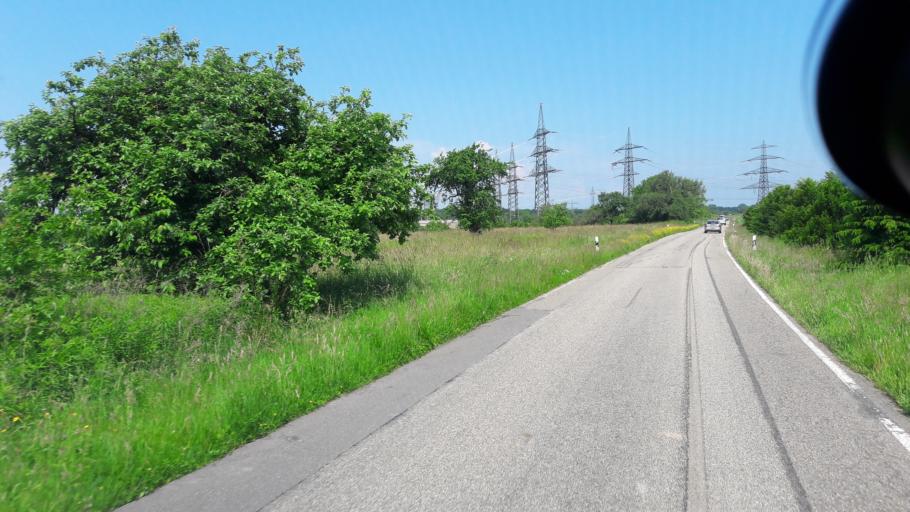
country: DE
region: Baden-Wuerttemberg
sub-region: Karlsruhe Region
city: Kuppenheim
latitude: 48.8445
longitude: 8.2523
